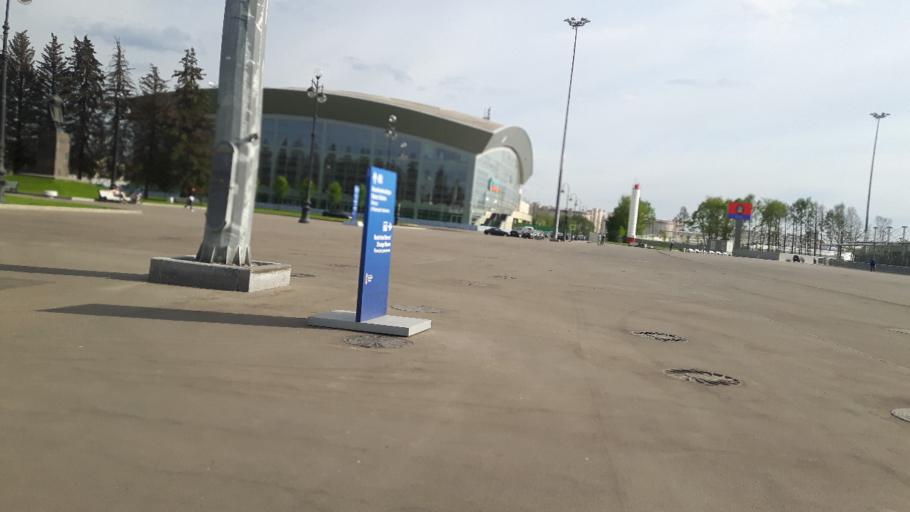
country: RU
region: St.-Petersburg
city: Staraya Derevnya
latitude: 59.9733
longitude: 30.2258
